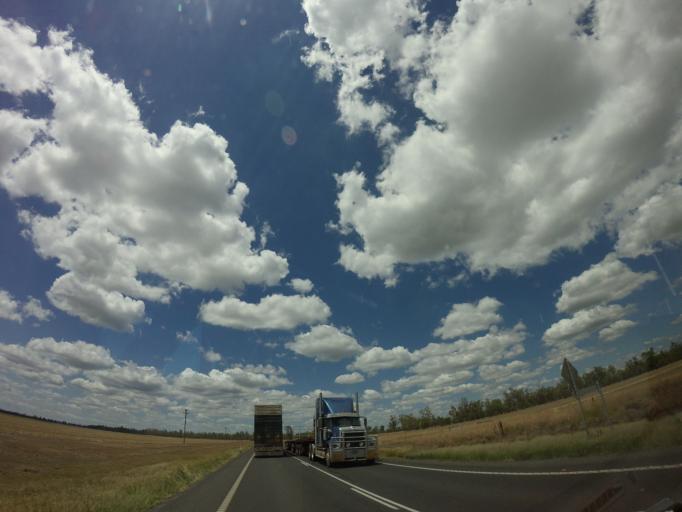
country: AU
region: Queensland
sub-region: Toowoomba
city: Oakey
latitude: -27.8157
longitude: 151.3577
